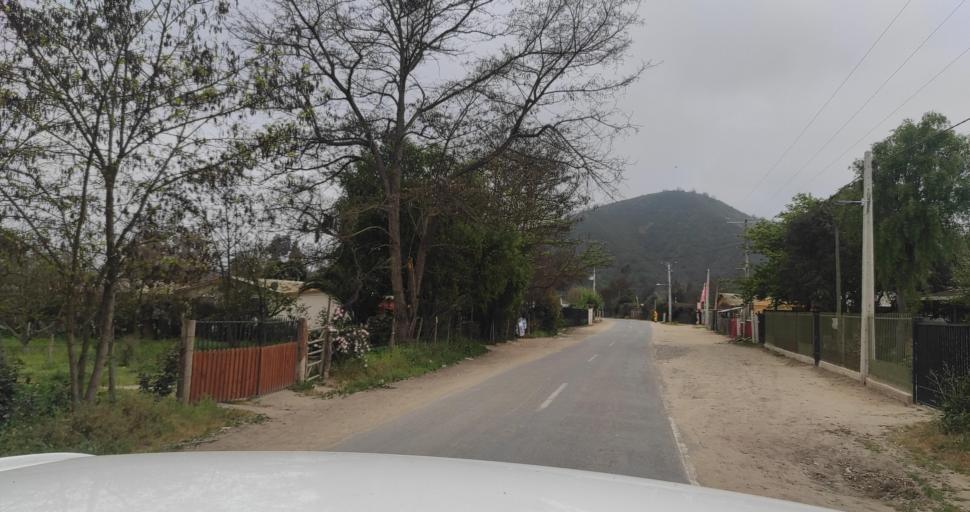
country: CL
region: Valparaiso
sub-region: Provincia de Marga Marga
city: Villa Alemana
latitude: -33.3606
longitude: -71.3019
